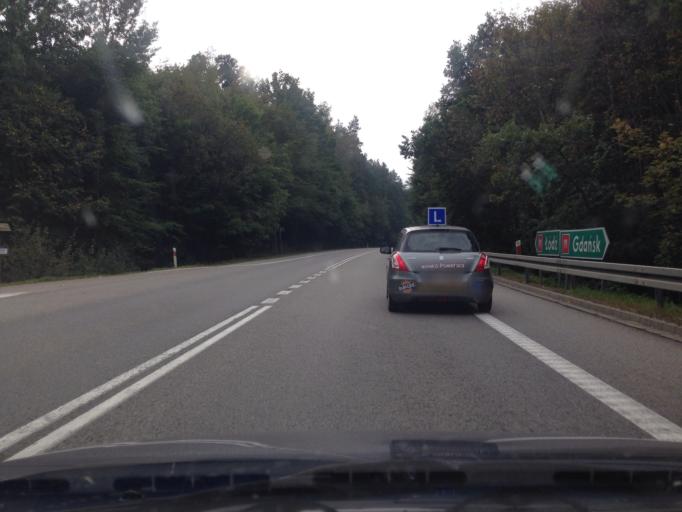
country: PL
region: Pomeranian Voivodeship
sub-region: Powiat starogardzki
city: Smetowo Graniczne
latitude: 53.7457
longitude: 18.7506
